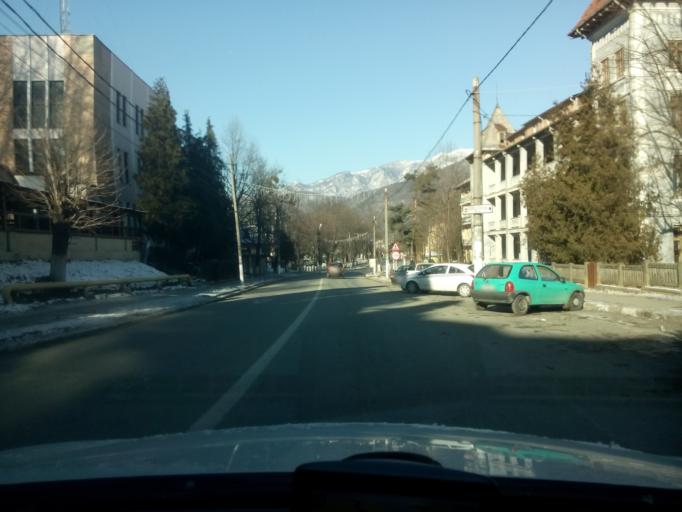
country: RO
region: Valcea
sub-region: Oras Calimanesti
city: Jiblea Veche
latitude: 45.2455
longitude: 24.3392
